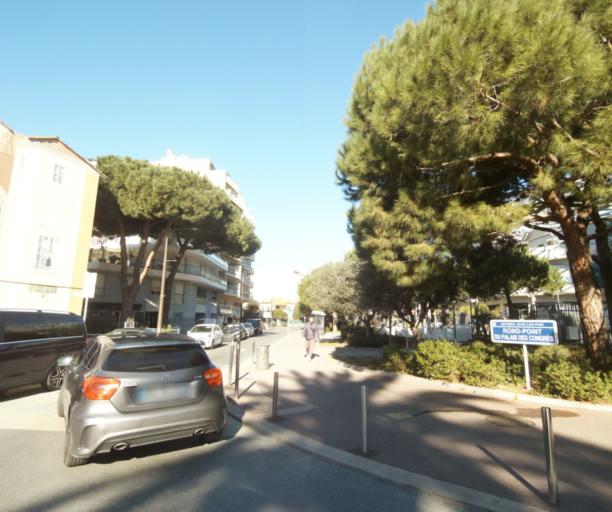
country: FR
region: Provence-Alpes-Cote d'Azur
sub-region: Departement des Alpes-Maritimes
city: Antibes
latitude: 43.5680
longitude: 7.1156
